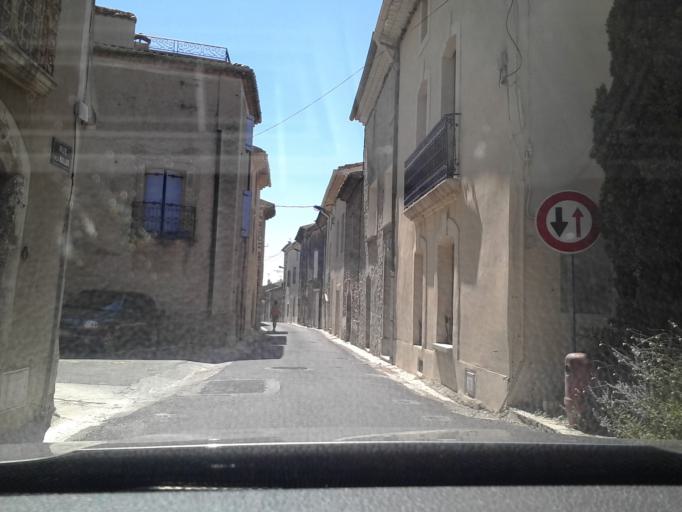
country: FR
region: Languedoc-Roussillon
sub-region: Departement de l'Herault
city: Montpeyroux
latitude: 43.7004
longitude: 3.4984
